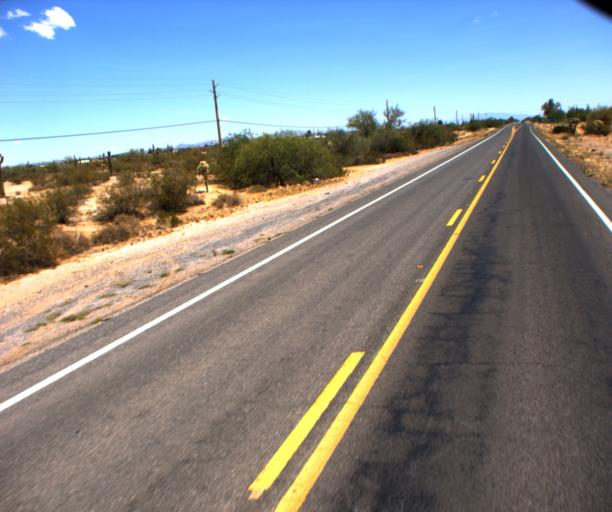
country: US
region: Arizona
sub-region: Pinal County
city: Florence
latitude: 32.9619
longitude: -111.3368
